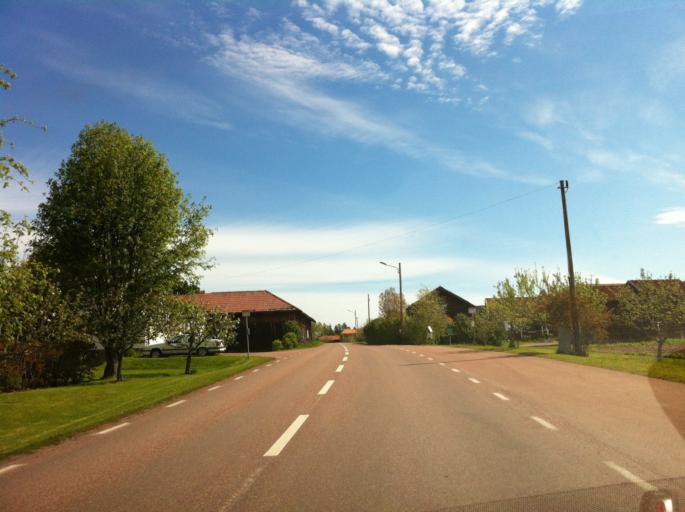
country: SE
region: Dalarna
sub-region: Mora Kommun
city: Mora
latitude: 60.9074
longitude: 14.6097
